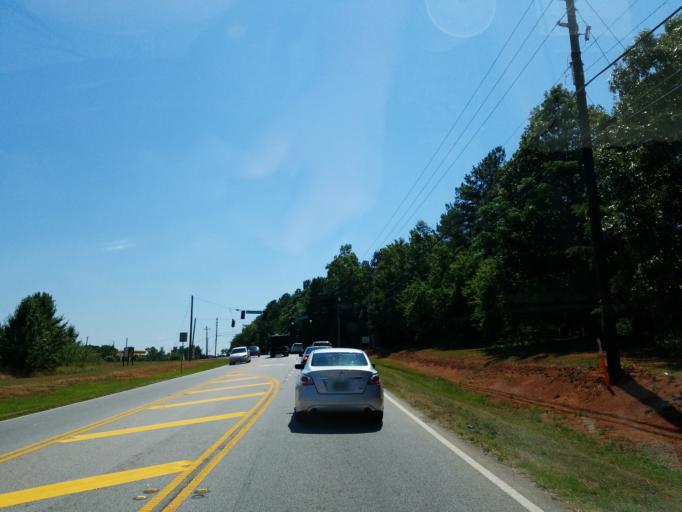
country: US
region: Georgia
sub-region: Clayton County
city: Lovejoy
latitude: 33.4538
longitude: -84.3099
